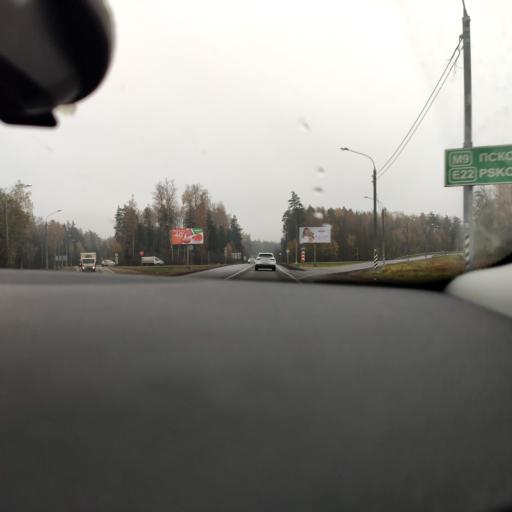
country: RU
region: Moskovskaya
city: Petrovo-Dal'neye
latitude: 55.7849
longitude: 37.1587
